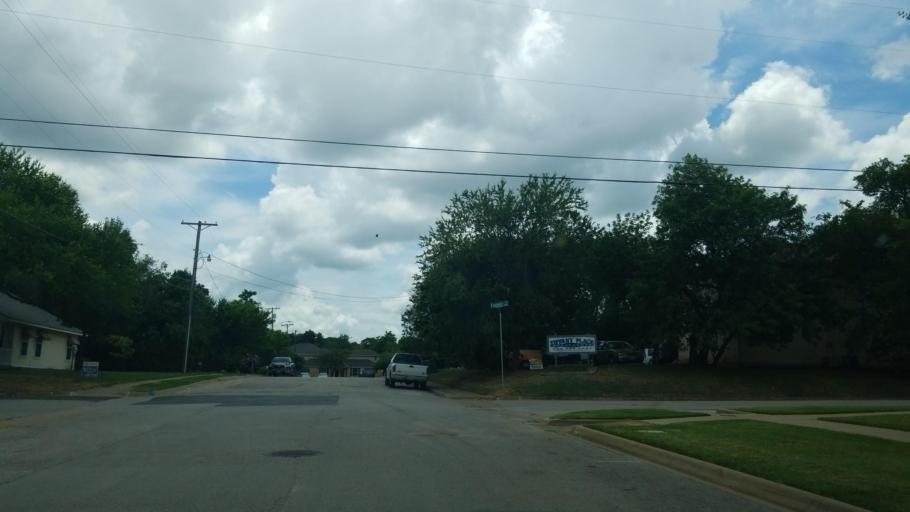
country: US
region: Texas
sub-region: Denton County
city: Denton
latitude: 33.2056
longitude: -97.1444
